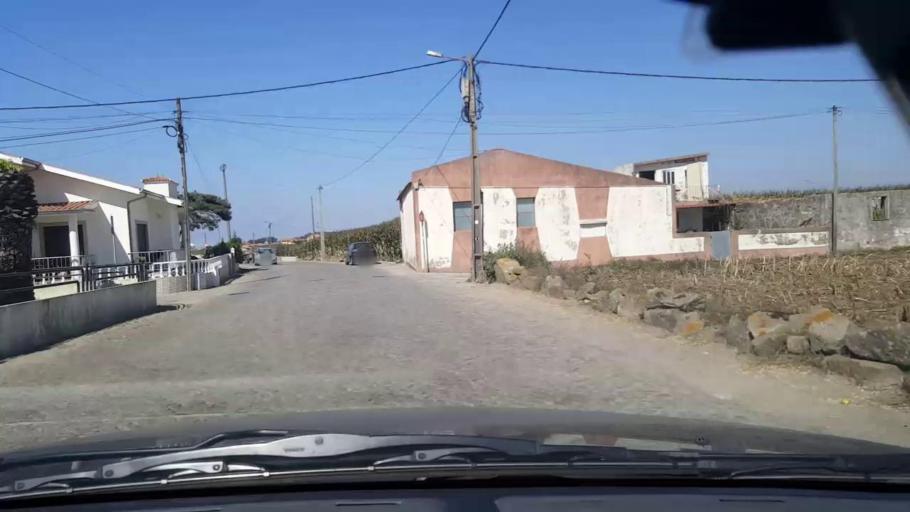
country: PT
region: Porto
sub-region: Matosinhos
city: Lavra
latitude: 41.2844
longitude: -8.7241
